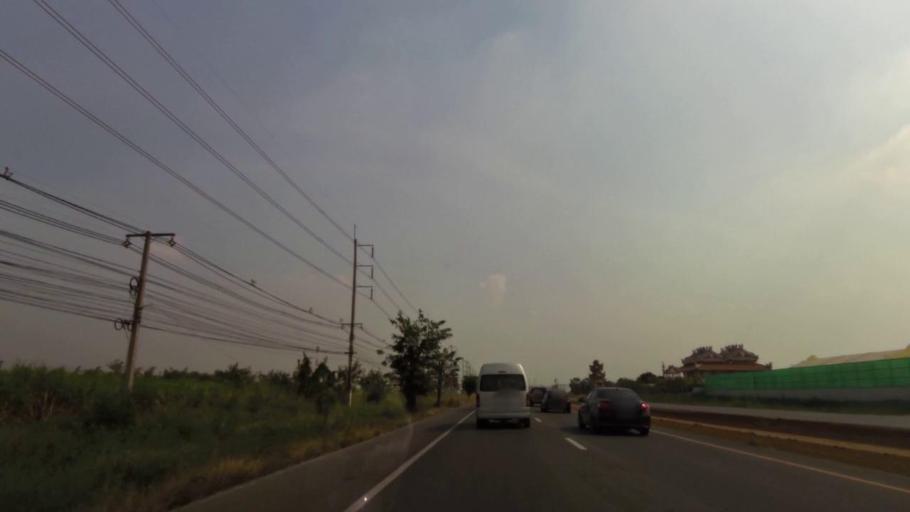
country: TH
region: Chon Buri
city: Ban Bueng
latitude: 13.2930
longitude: 101.1687
